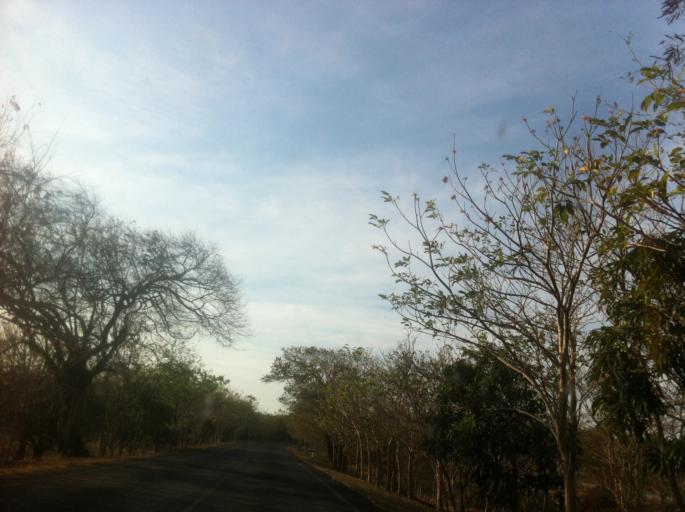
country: NI
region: Rivas
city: San Juan del Sur
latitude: 11.2932
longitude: -85.6827
